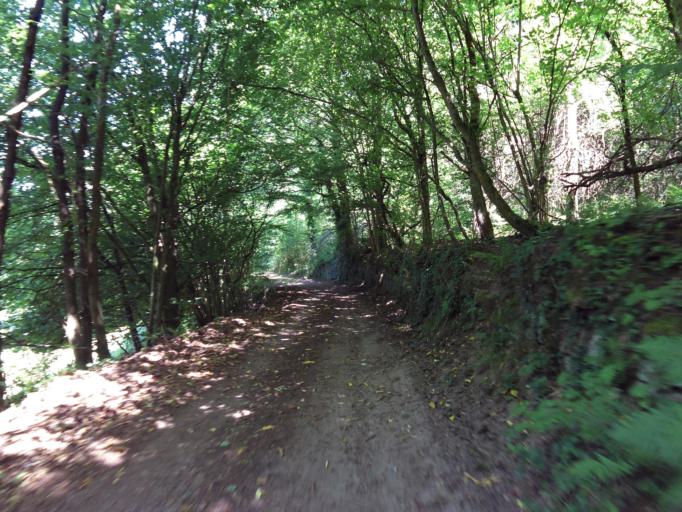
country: DE
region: Rheinland-Pfalz
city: Frankeneck
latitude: 49.3704
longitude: 8.0477
